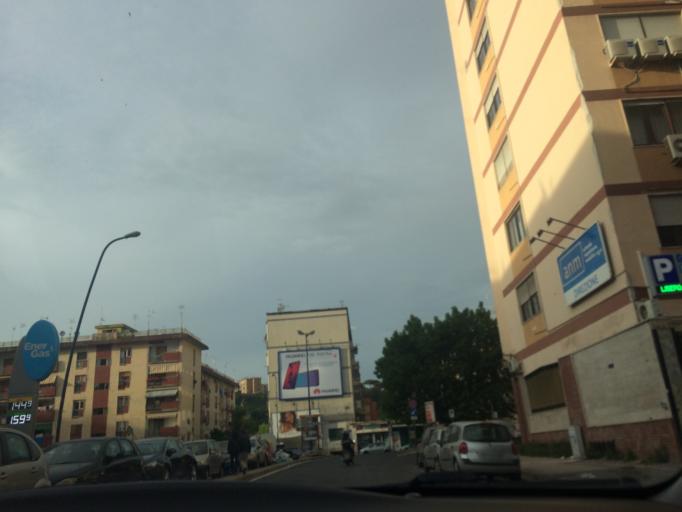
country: IT
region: Campania
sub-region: Provincia di Napoli
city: Bagnoli
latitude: 40.8292
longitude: 14.1962
